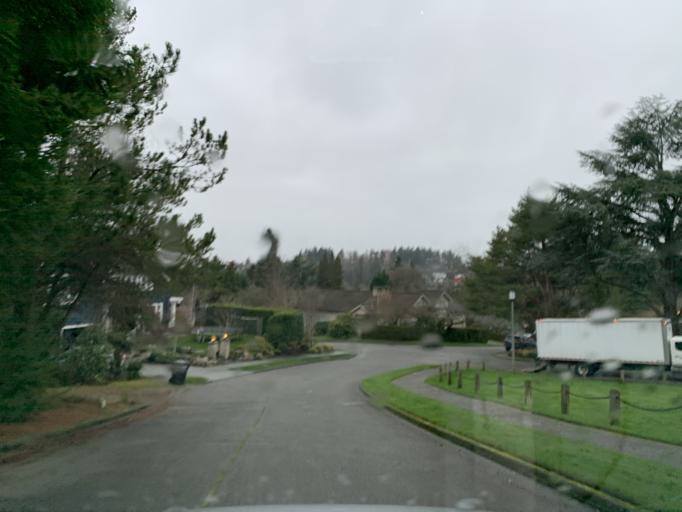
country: US
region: Washington
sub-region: King County
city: Yarrow Point
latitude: 47.6687
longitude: -122.2628
